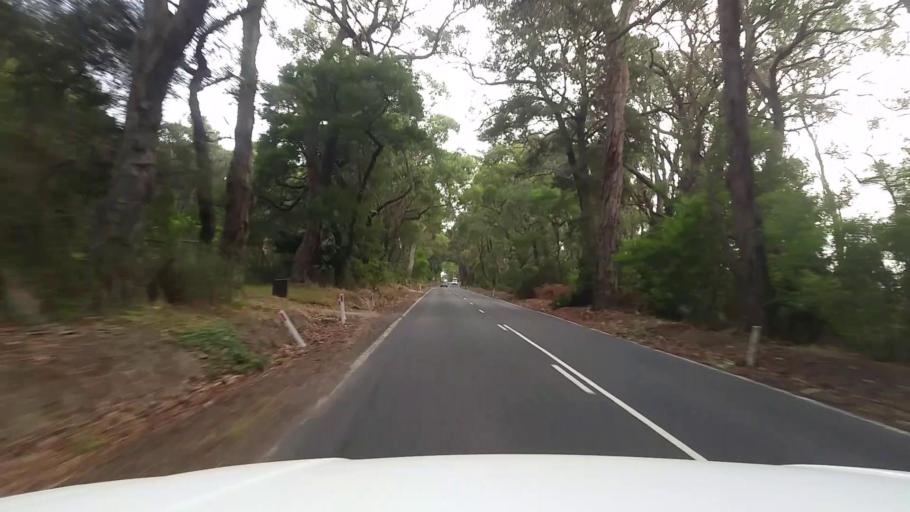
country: AU
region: Victoria
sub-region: Mornington Peninsula
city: Balnarring
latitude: -38.3370
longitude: 145.0964
